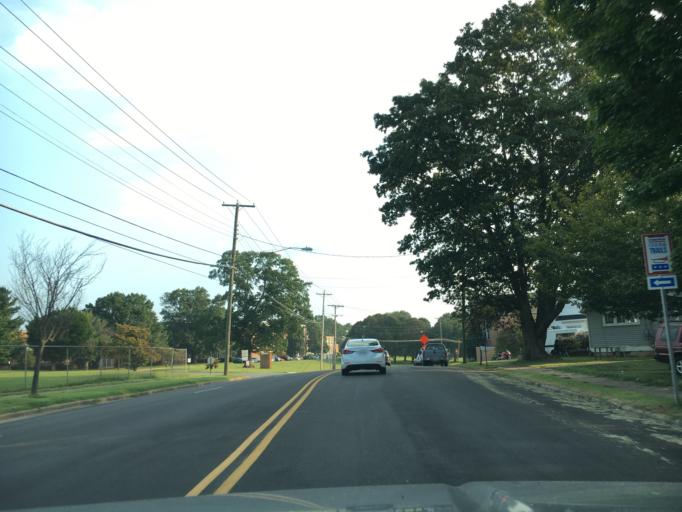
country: US
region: Virginia
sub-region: City of Lynchburg
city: West Lynchburg
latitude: 37.4050
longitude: -79.1666
